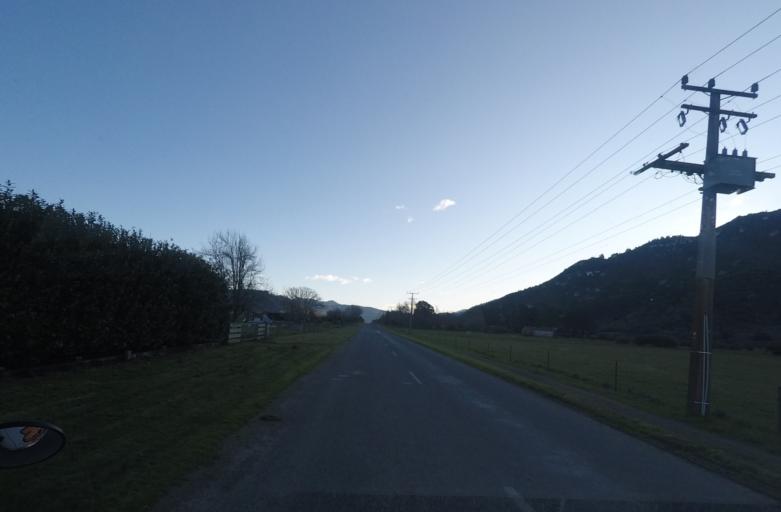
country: NZ
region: Marlborough
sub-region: Marlborough District
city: Picton
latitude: -41.2901
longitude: 173.8927
